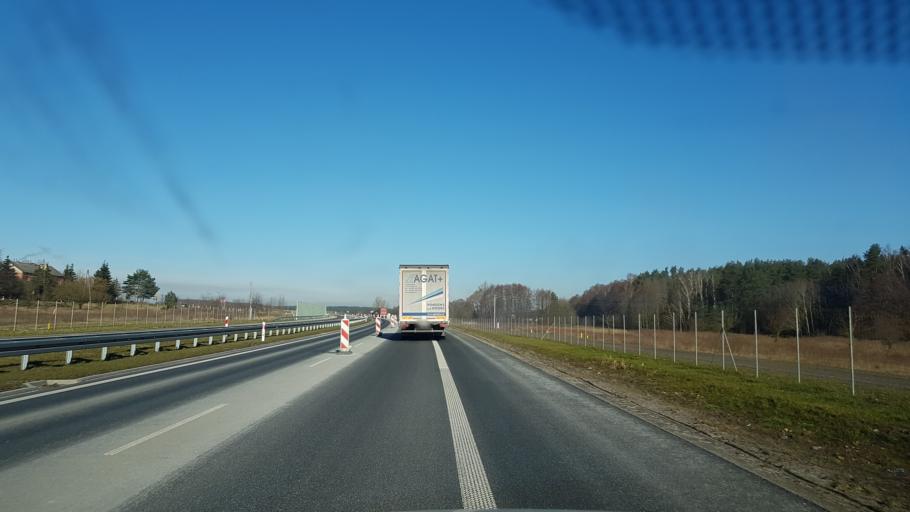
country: PL
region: West Pomeranian Voivodeship
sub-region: Powiat goleniowski
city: Przybiernow
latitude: 53.8102
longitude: 14.7694
